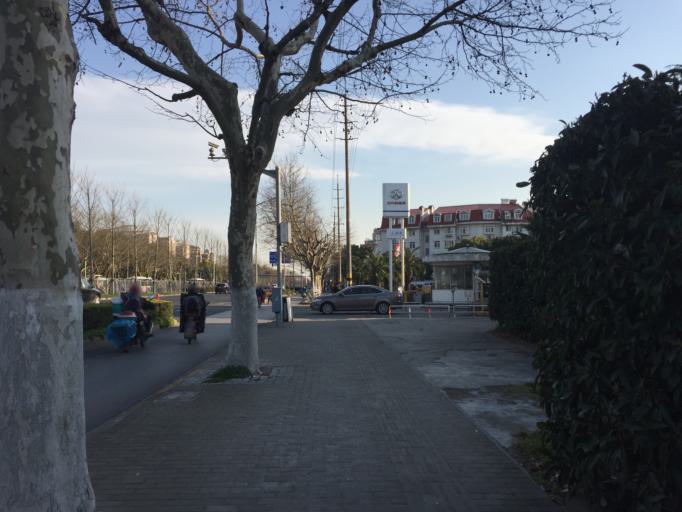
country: CN
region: Shanghai Shi
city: Huamu
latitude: 31.1886
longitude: 121.5359
